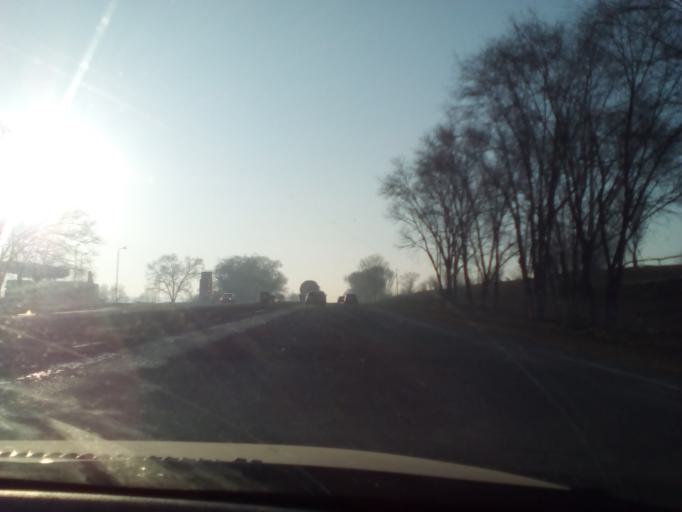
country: KZ
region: Almaty Oblysy
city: Burunday
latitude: 43.2227
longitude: 76.5776
